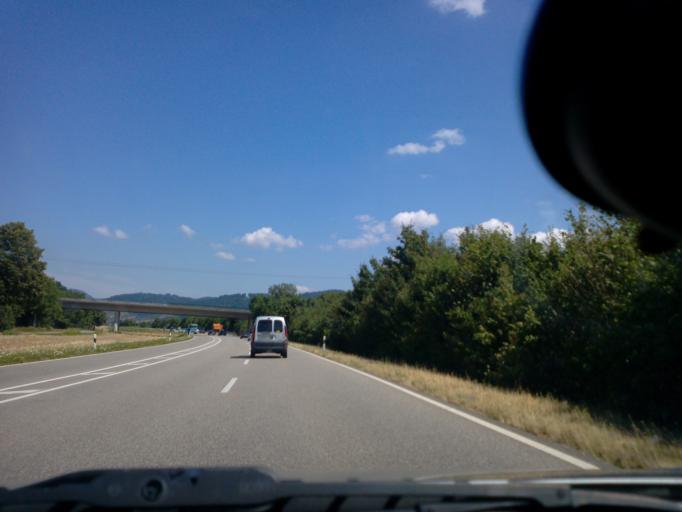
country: DE
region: Baden-Wuerttemberg
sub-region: Freiburg Region
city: Biberach
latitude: 48.3628
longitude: 8.0232
